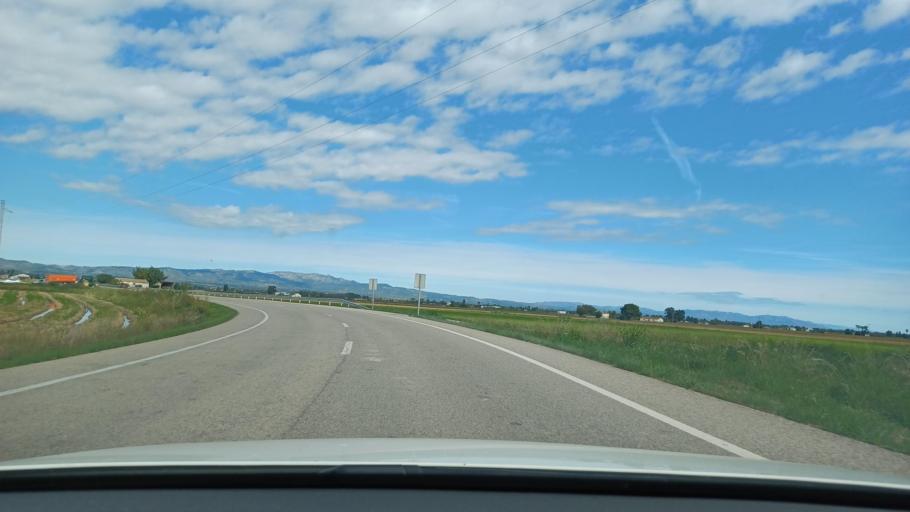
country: ES
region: Catalonia
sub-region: Provincia de Tarragona
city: Deltebre
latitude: 40.6927
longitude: 0.6832
